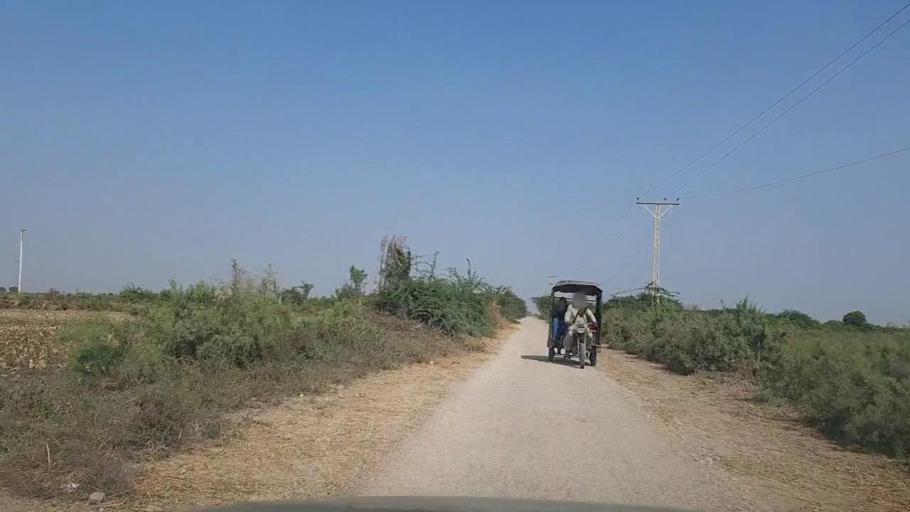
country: PK
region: Sindh
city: Thatta
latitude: 24.6016
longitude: 67.9528
